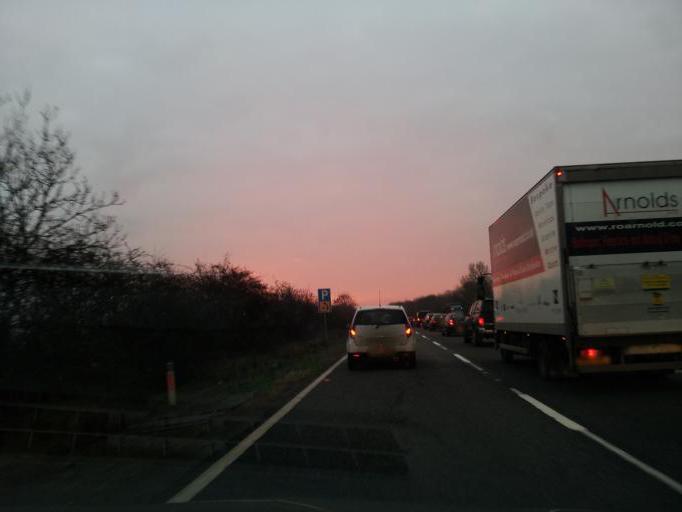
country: GB
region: England
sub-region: Peterborough
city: Wittering
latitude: 52.6077
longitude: -0.4321
